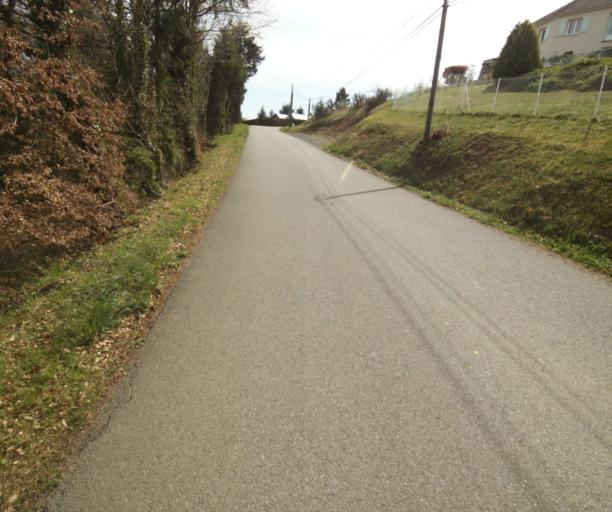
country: FR
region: Limousin
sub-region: Departement de la Correze
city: Naves
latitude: 45.3078
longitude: 1.7658
